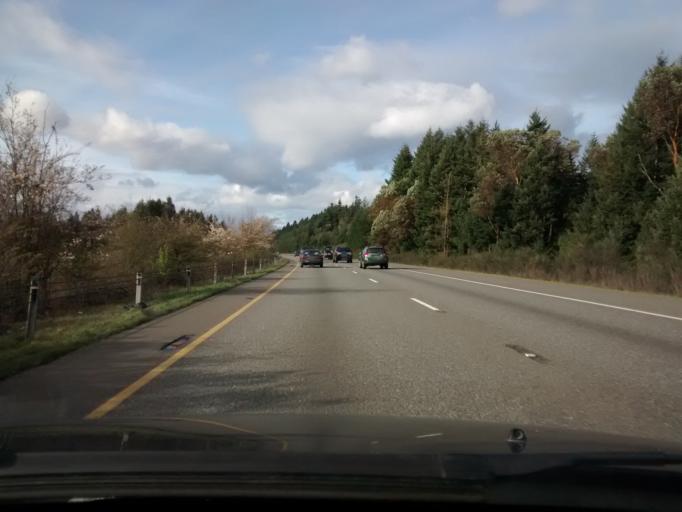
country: US
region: Washington
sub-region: Pierce County
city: Purdy
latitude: 47.3787
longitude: -122.6157
